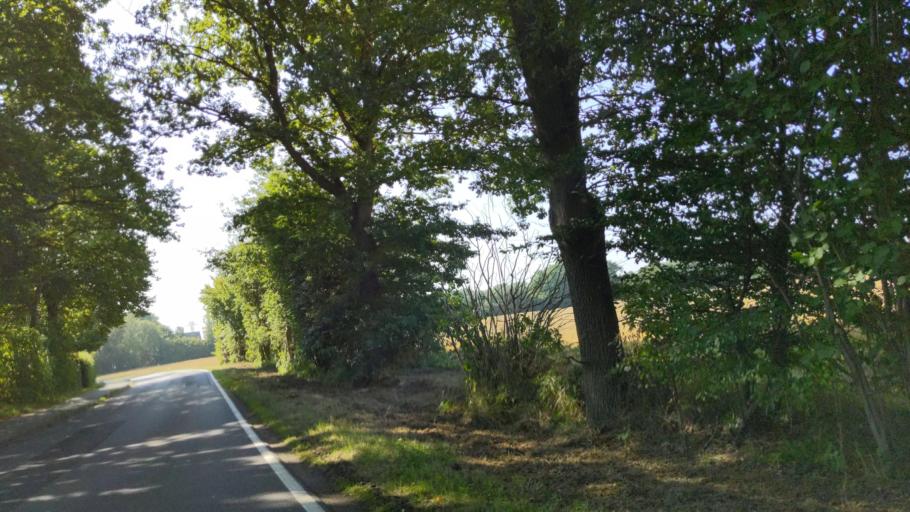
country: DE
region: Schleswig-Holstein
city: Gross Schenkenberg
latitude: 53.7983
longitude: 10.5813
